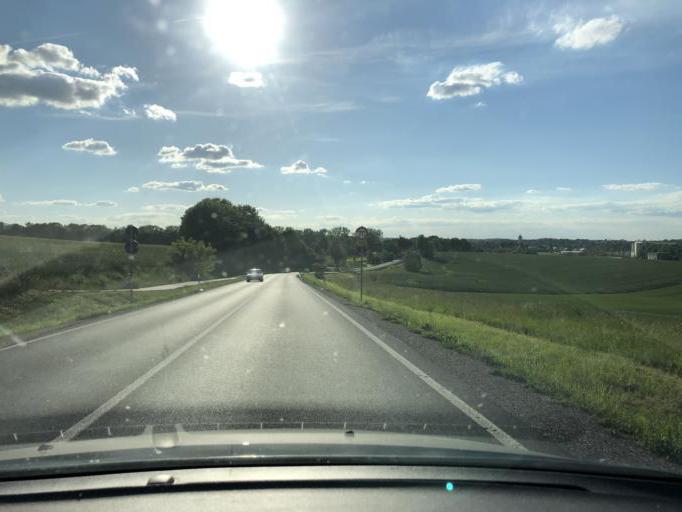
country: DE
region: Thuringia
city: Lodla
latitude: 51.0015
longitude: 12.4019
